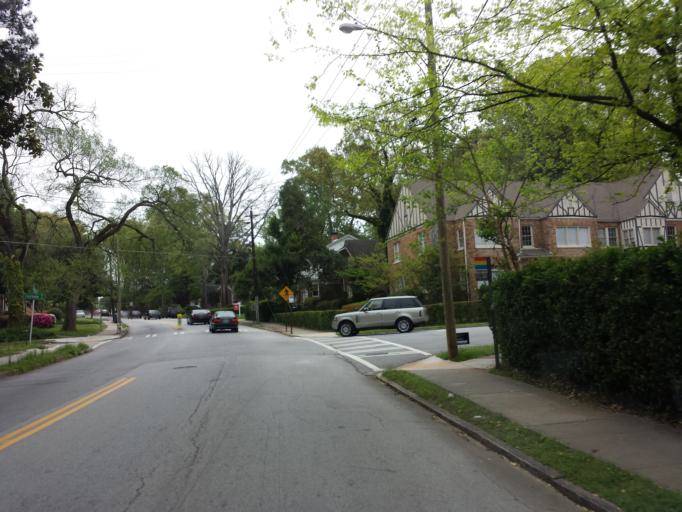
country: US
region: Georgia
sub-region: DeKalb County
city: Druid Hills
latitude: 33.7901
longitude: -84.3557
